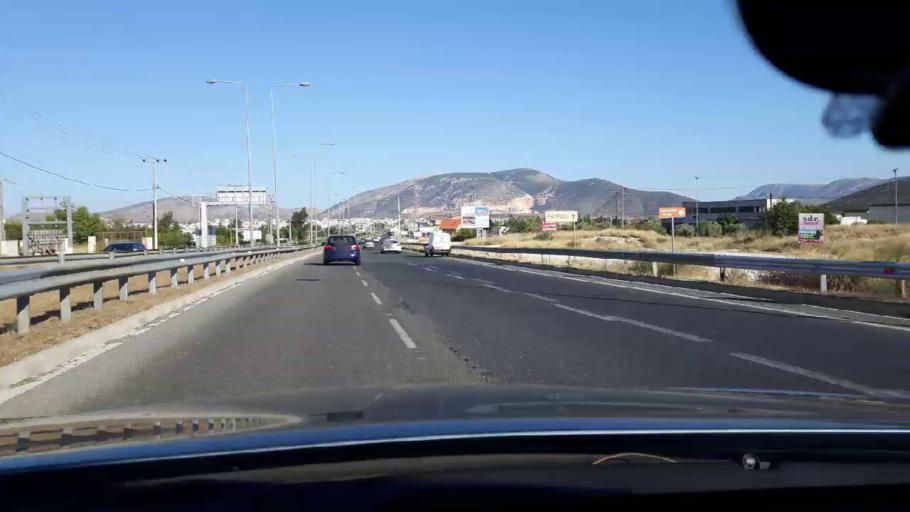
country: GR
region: Attica
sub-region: Nomarchia Anatolikis Attikis
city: Markopoulo
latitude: 37.8923
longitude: 23.9172
